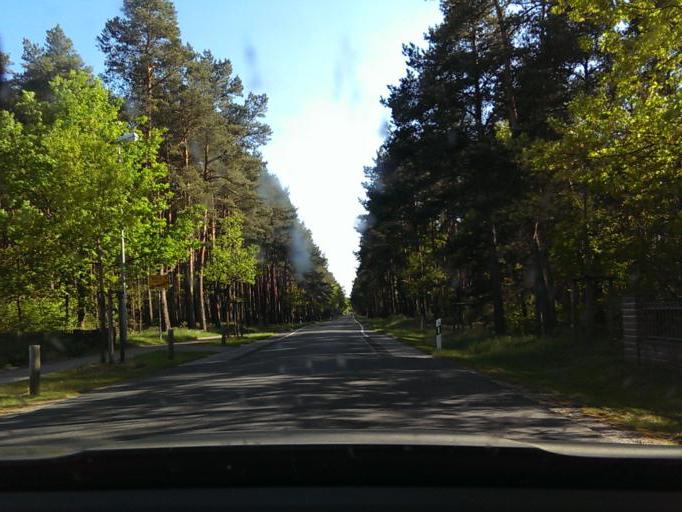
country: DE
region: Lower Saxony
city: Wietze
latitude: 52.6695
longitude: 9.8388
